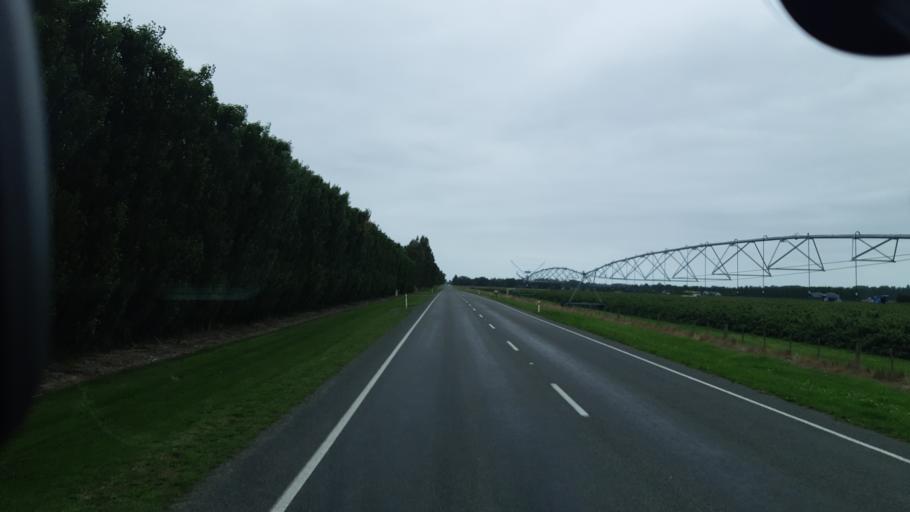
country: NZ
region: Canterbury
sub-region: Ashburton District
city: Ashburton
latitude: -43.8134
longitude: 171.6993
